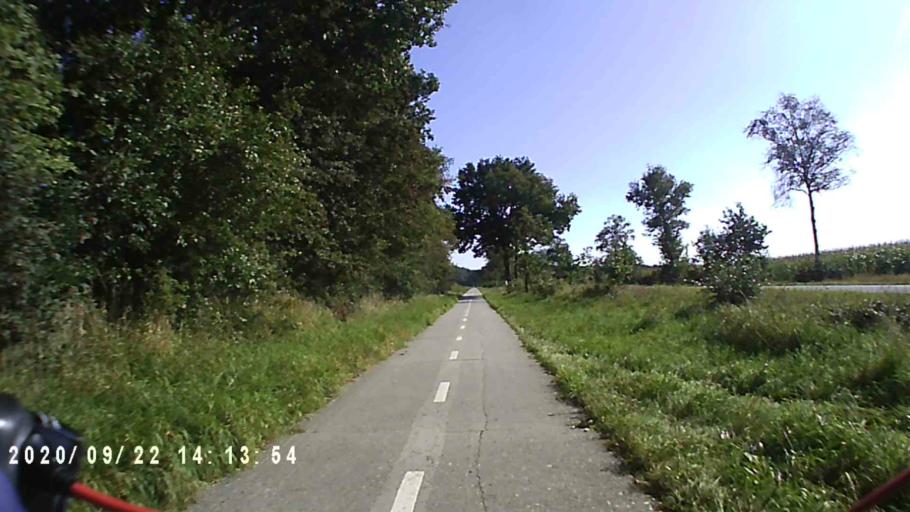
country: NL
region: Groningen
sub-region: Gemeente Leek
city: Leek
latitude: 53.0733
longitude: 6.4185
